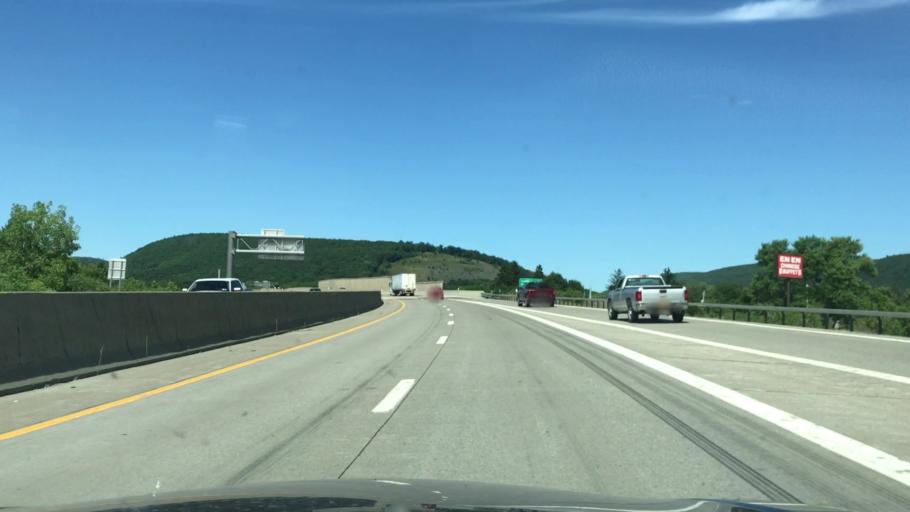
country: US
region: New York
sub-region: Steuben County
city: Painted Post
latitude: 42.1539
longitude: -77.0810
